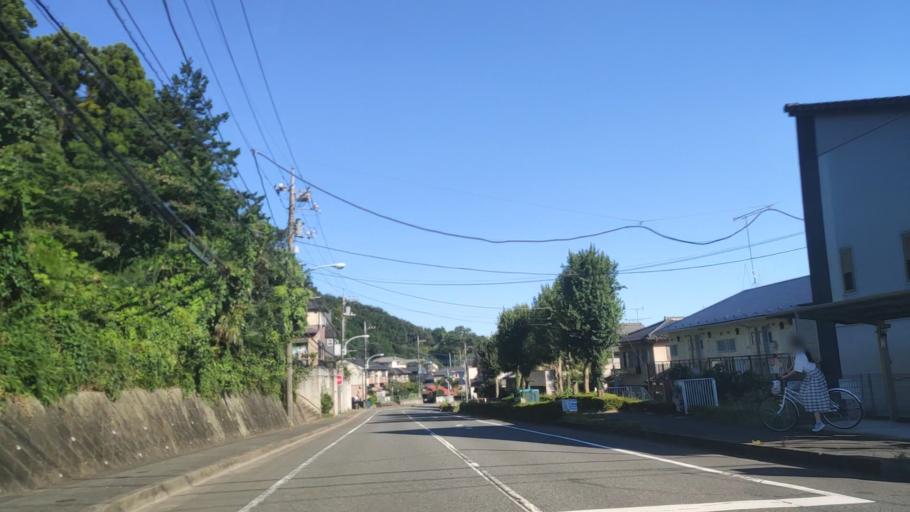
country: JP
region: Tokyo
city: Hachioji
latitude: 35.6094
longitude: 139.3131
